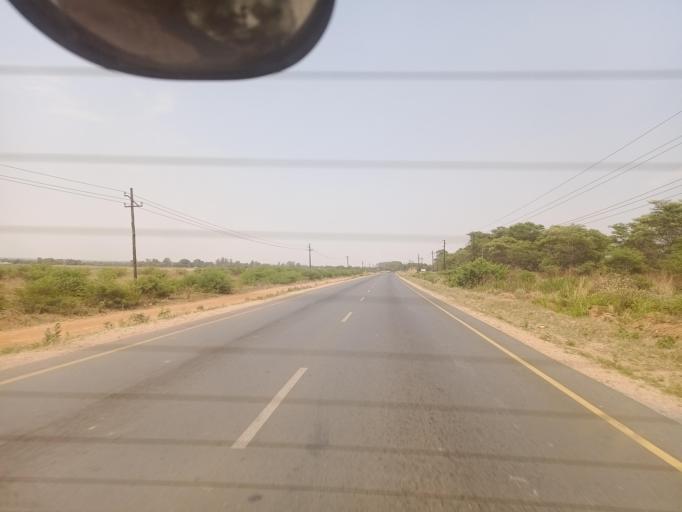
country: ZM
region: Lusaka
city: Lusaka
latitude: -15.2694
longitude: 28.4149
